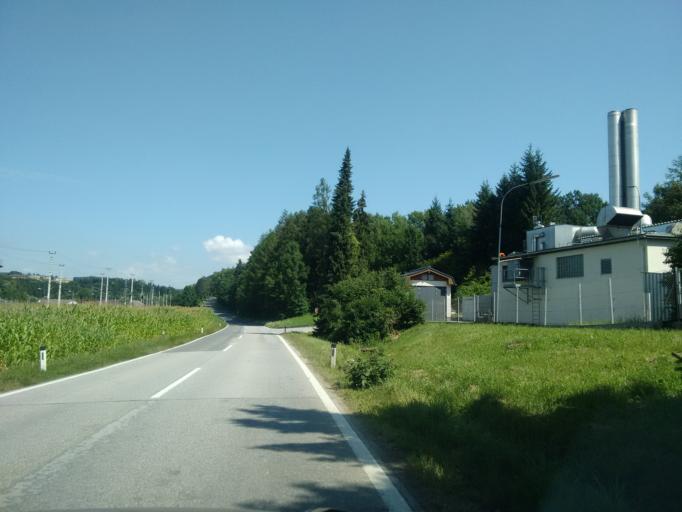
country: AT
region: Upper Austria
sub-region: Politischer Bezirk Kirchdorf an der Krems
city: Kremsmunster
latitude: 48.0223
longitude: 14.1213
